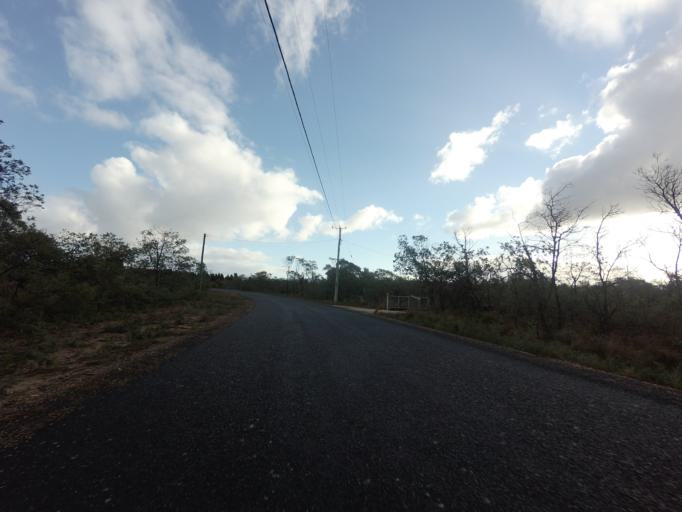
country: AU
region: Tasmania
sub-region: Break O'Day
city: St Helens
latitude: -42.1022
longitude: 148.0739
